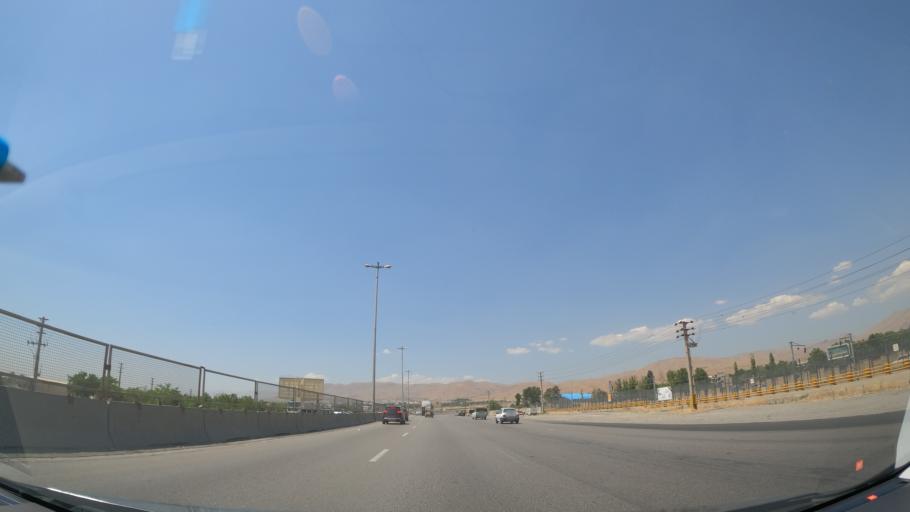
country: IR
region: Alborz
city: Karaj
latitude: 35.8526
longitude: 50.9089
